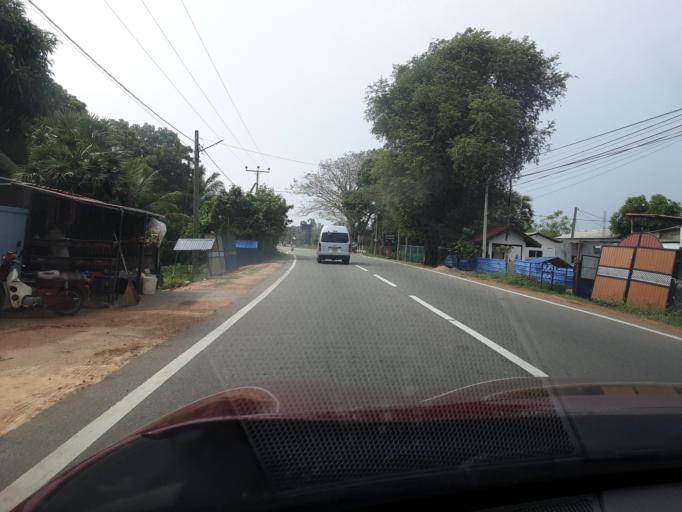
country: LK
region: Northern Province
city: Jaffna
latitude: 9.6606
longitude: 80.0526
